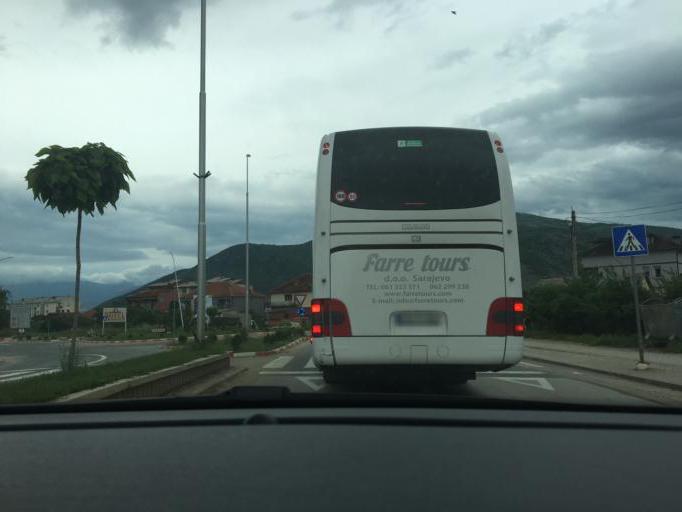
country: MK
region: Kicevo
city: Kicevo
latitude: 41.5007
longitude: 20.9520
